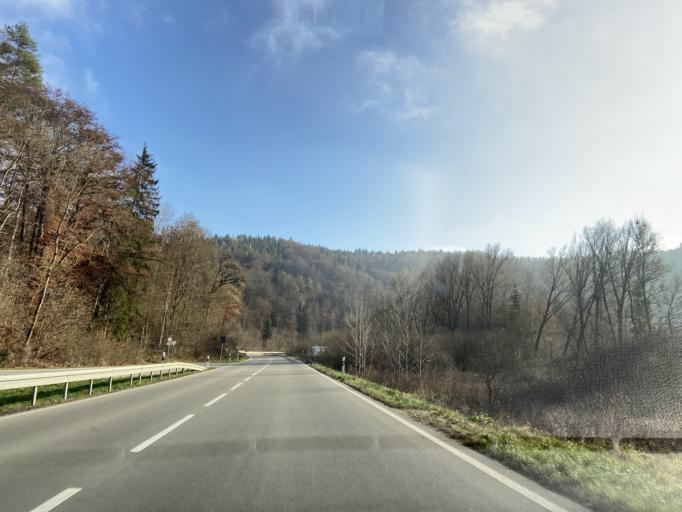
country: DE
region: Baden-Wuerttemberg
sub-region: Tuebingen Region
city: Veringenstadt
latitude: 48.1887
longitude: 9.2209
